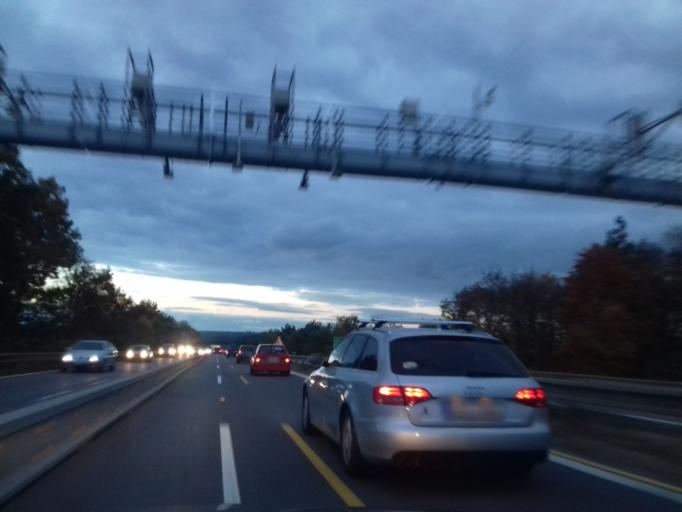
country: CZ
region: Central Bohemia
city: Trhovy Stepanov
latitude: 49.7284
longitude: 15.0459
